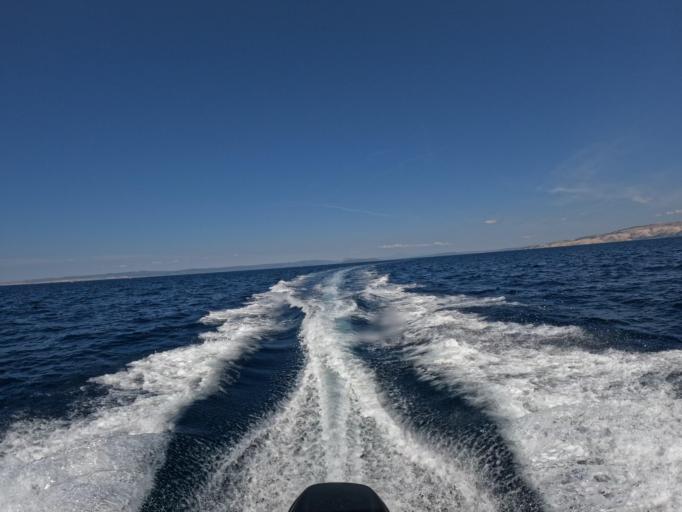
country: HR
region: Primorsko-Goranska
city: Lopar
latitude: 44.8744
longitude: 14.6639
